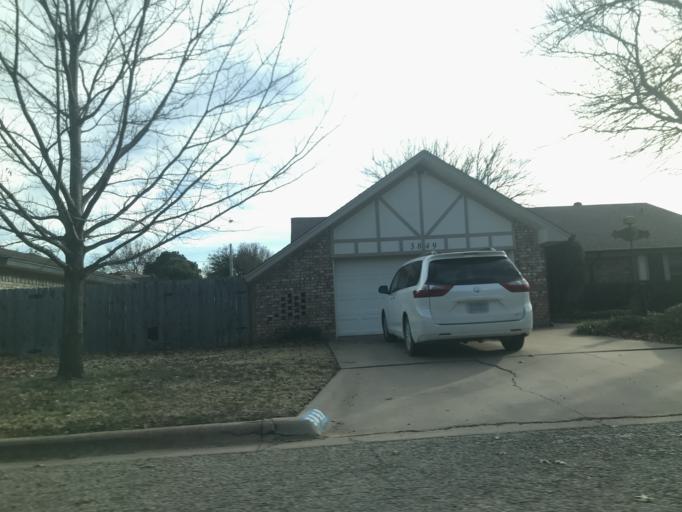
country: US
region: Texas
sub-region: Taylor County
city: Abilene
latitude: 32.3900
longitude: -99.7732
